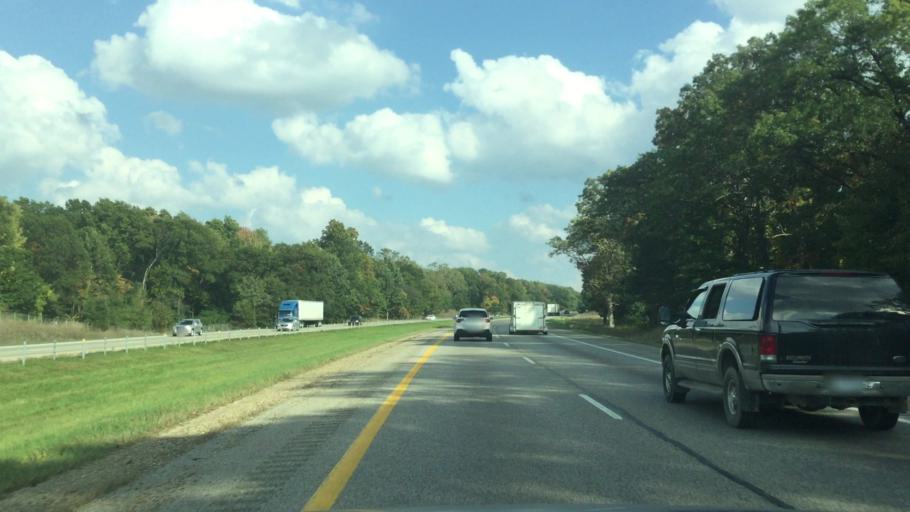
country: US
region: Michigan
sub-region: Kalamazoo County
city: Galesburg
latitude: 42.2824
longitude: -85.3507
